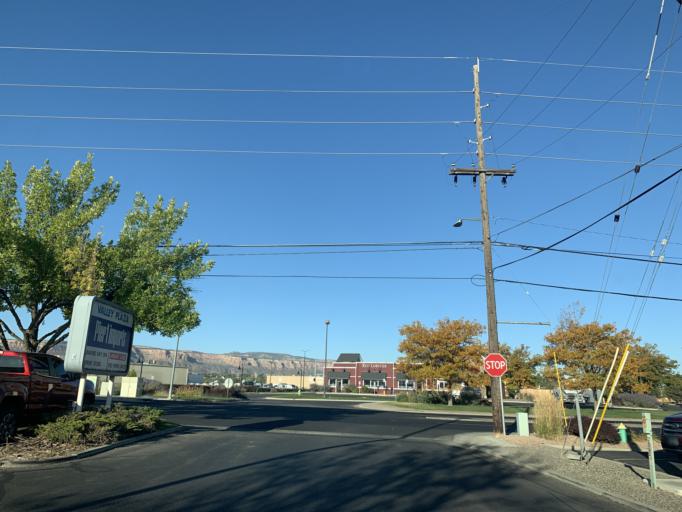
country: US
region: Colorado
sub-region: Mesa County
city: Redlands
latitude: 39.0882
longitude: -108.5985
